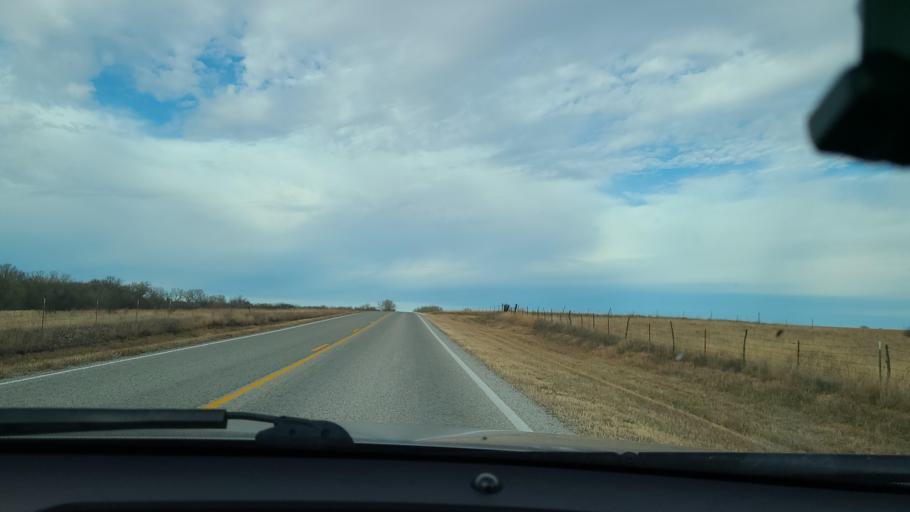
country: US
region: Kansas
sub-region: McPherson County
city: Inman
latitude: 38.3399
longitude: -97.9245
